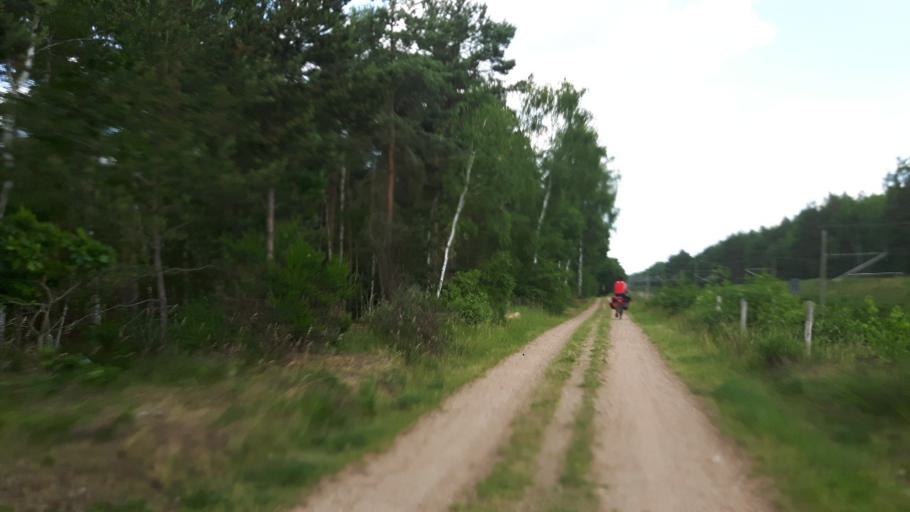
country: DE
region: Saxony-Anhalt
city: Radis
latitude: 51.7776
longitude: 12.5375
